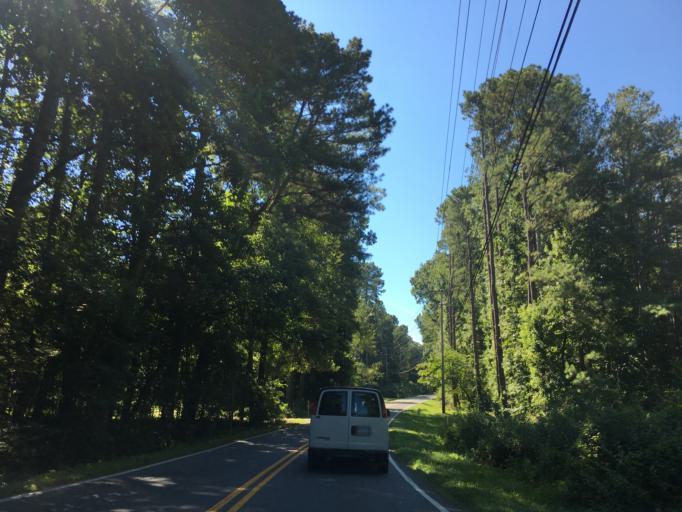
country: US
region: Georgia
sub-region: Fulton County
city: Milton
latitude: 34.1579
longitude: -84.2872
